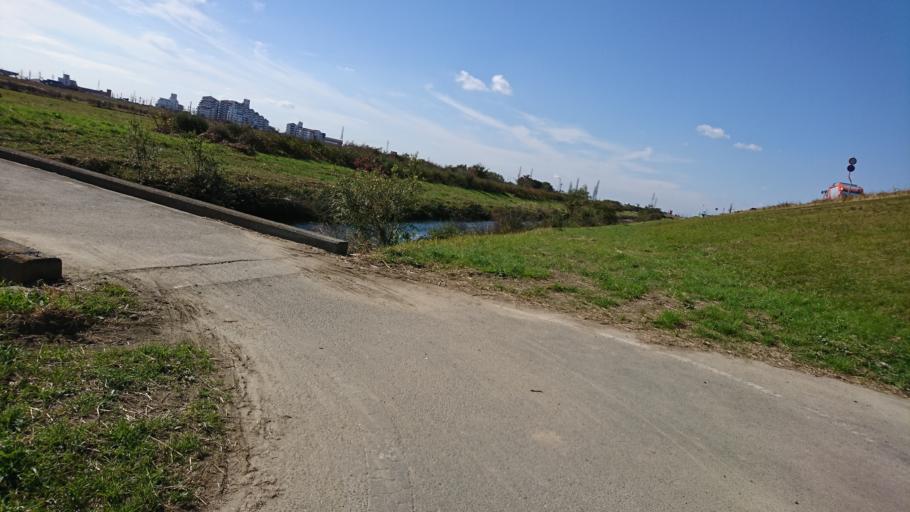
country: JP
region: Hyogo
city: Kakogawacho-honmachi
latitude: 34.7738
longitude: 134.8254
